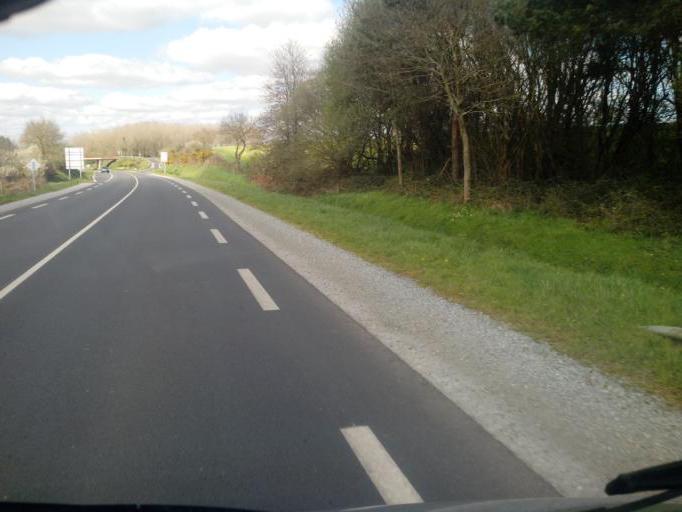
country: FR
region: Brittany
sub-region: Departement du Morbihan
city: Mauron
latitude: 48.0789
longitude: -2.2710
